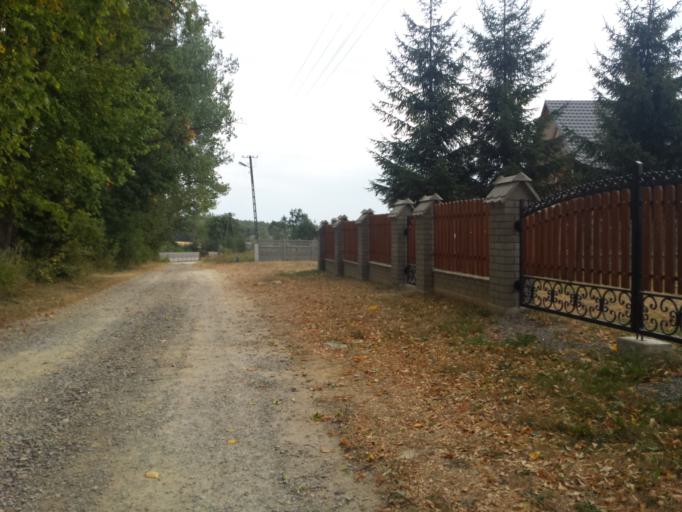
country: PL
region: Swietokrzyskie
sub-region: Powiat kielecki
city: Rakow
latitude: 50.6830
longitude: 21.0691
